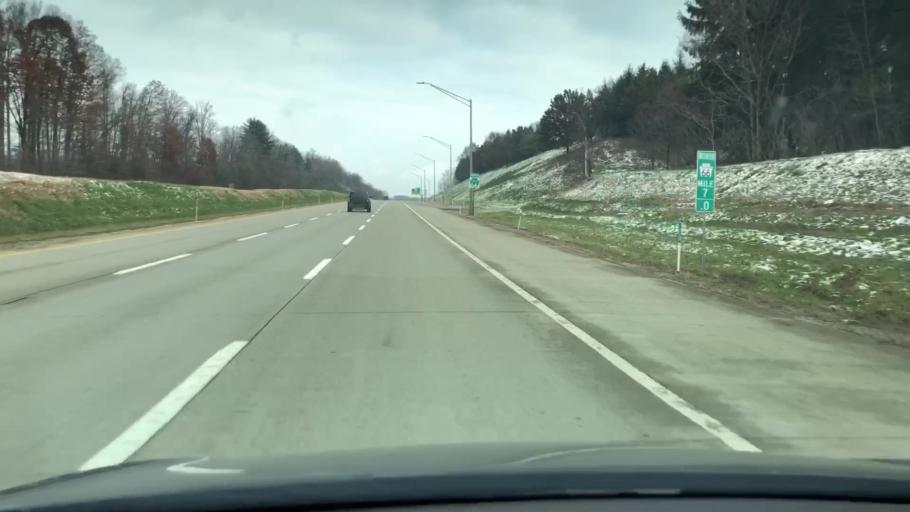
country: US
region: Pennsylvania
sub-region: Westmoreland County
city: Jeannette
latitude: 40.3157
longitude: -79.5884
